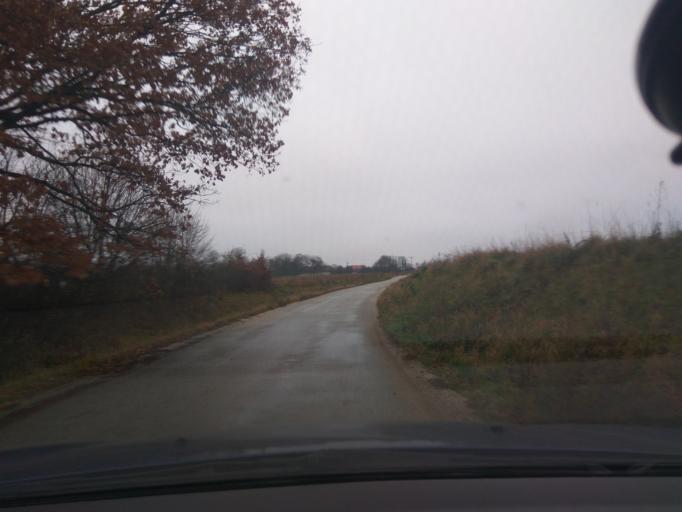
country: SK
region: Trnavsky
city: Vrbove
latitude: 48.6874
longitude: 17.6714
